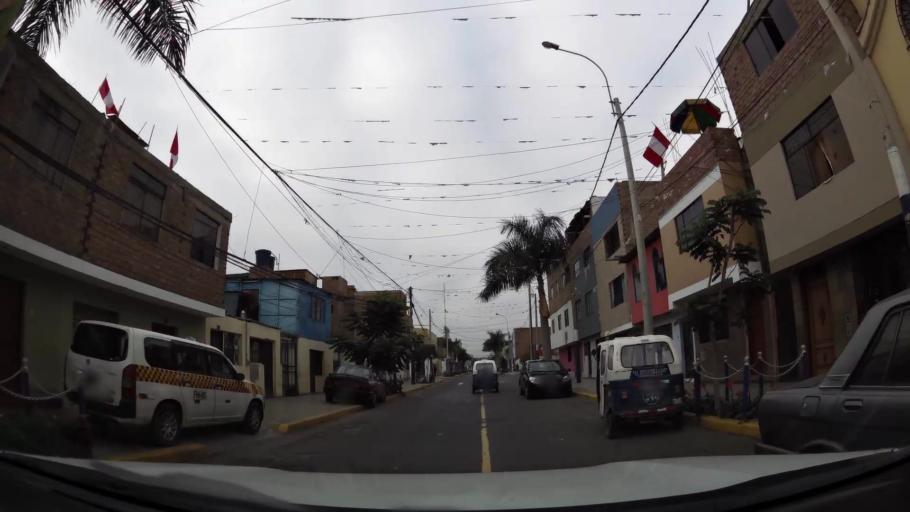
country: PE
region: Lima
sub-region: Lima
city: Surco
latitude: -12.1707
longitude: -77.0269
